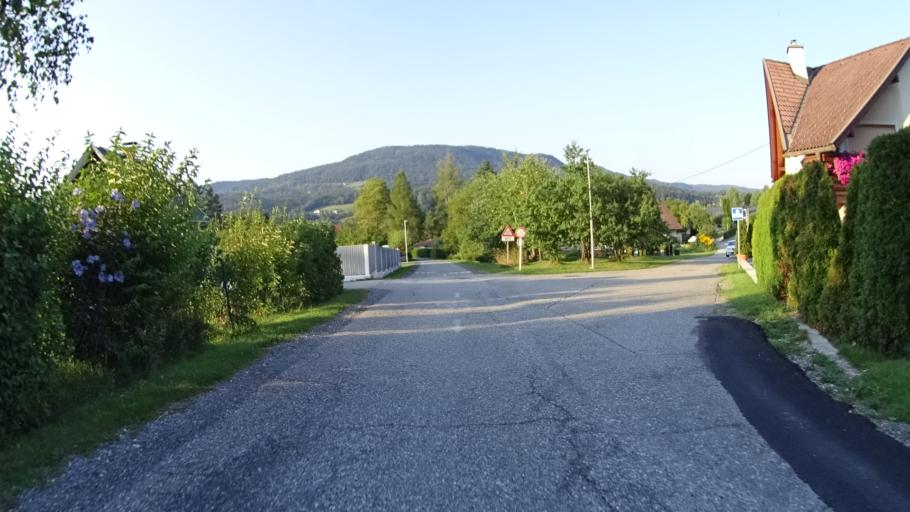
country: AT
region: Carinthia
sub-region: Politischer Bezirk Klagenfurt Land
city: Ludmannsdorf
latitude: 46.5317
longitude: 14.1051
